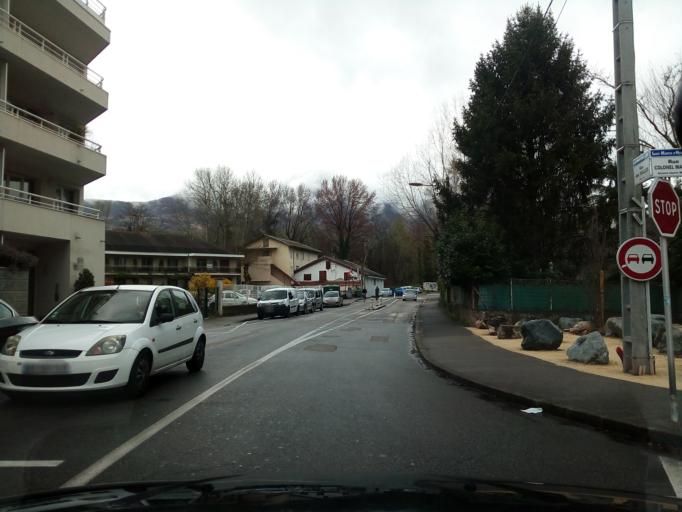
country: FR
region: Rhone-Alpes
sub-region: Departement de l'Isere
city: La Tronche
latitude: 45.1881
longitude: 5.7518
